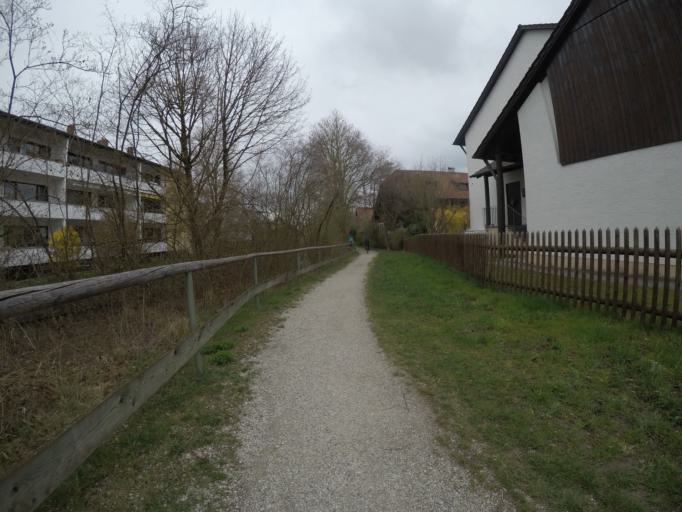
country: DE
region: Bavaria
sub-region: Lower Bavaria
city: Landshut
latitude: 48.5335
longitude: 12.1259
